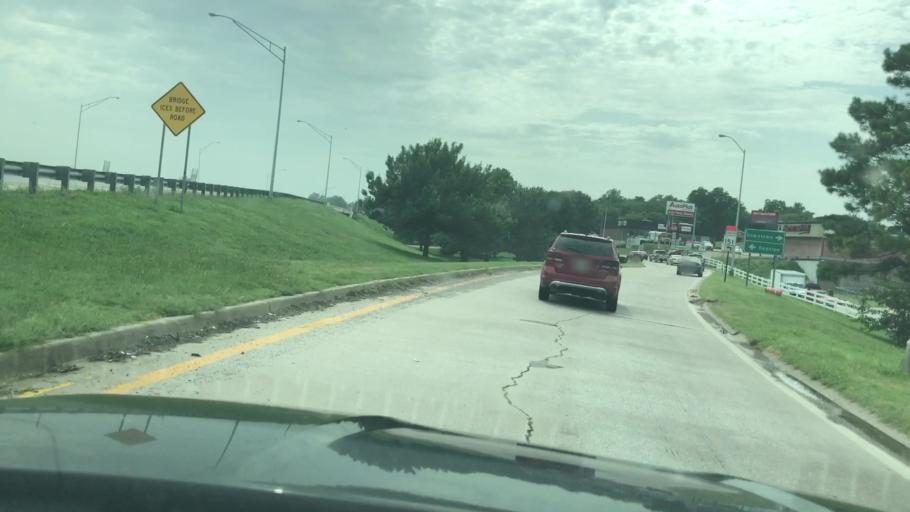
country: US
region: Oklahoma
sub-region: Tulsa County
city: Sand Springs
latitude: 36.1370
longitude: -96.1136
